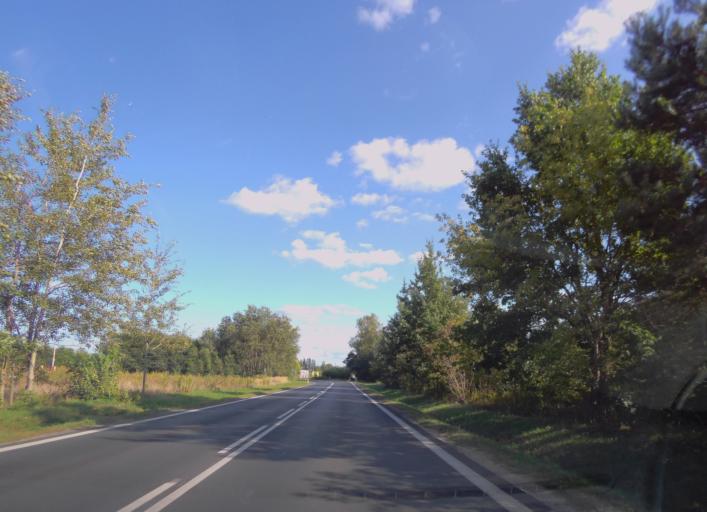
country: PL
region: Subcarpathian Voivodeship
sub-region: Tarnobrzeg
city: Tarnobrzeg
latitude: 50.5583
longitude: 21.7505
